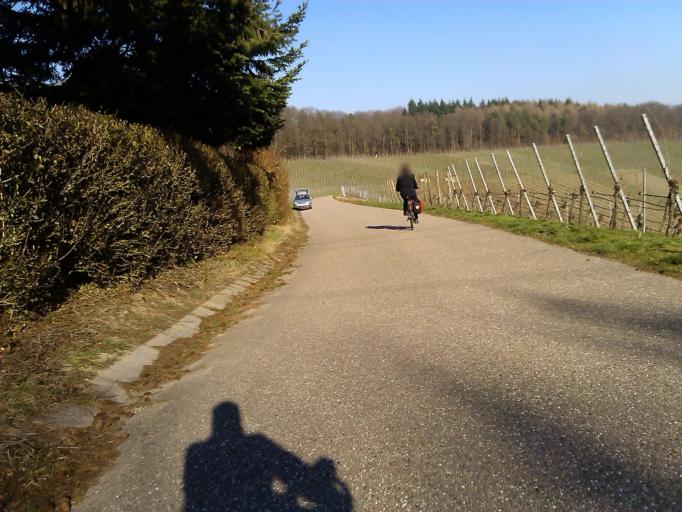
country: DE
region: Baden-Wuerttemberg
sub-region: Regierungsbezirk Stuttgart
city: Leingarten
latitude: 49.1233
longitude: 9.0874
